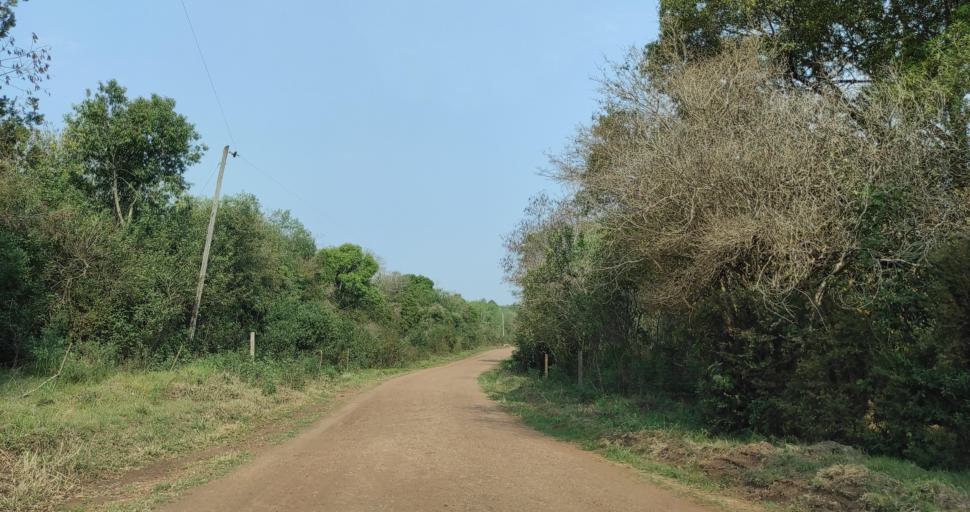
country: AR
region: Misiones
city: Cerro Cora
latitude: -27.5658
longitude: -55.5847
